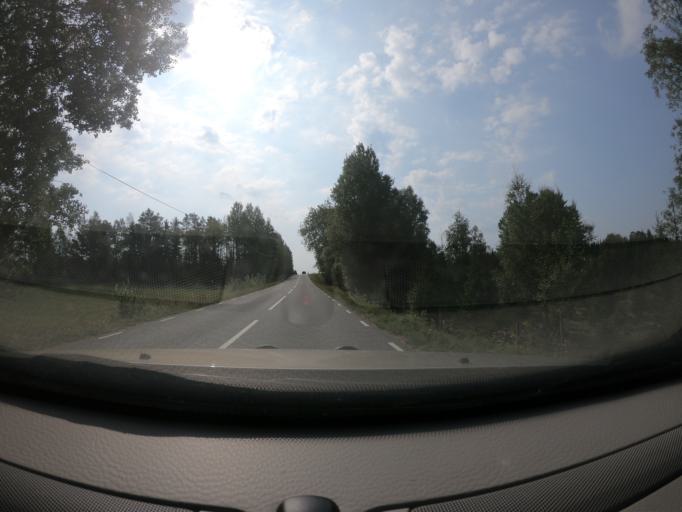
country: SE
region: Joenkoeping
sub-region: Vetlanda Kommun
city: Landsbro
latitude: 57.3016
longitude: 14.8701
